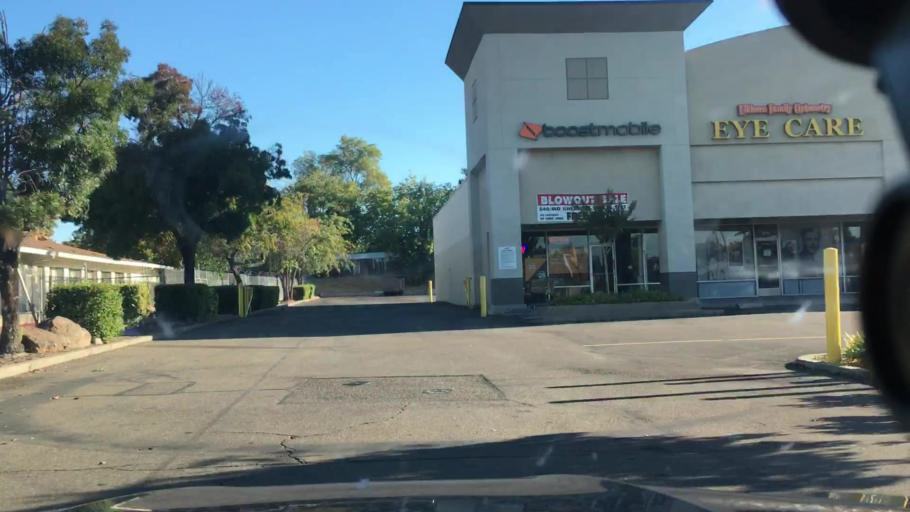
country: US
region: California
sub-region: Sacramento County
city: Foothill Farms
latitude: 38.6872
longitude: -121.3414
